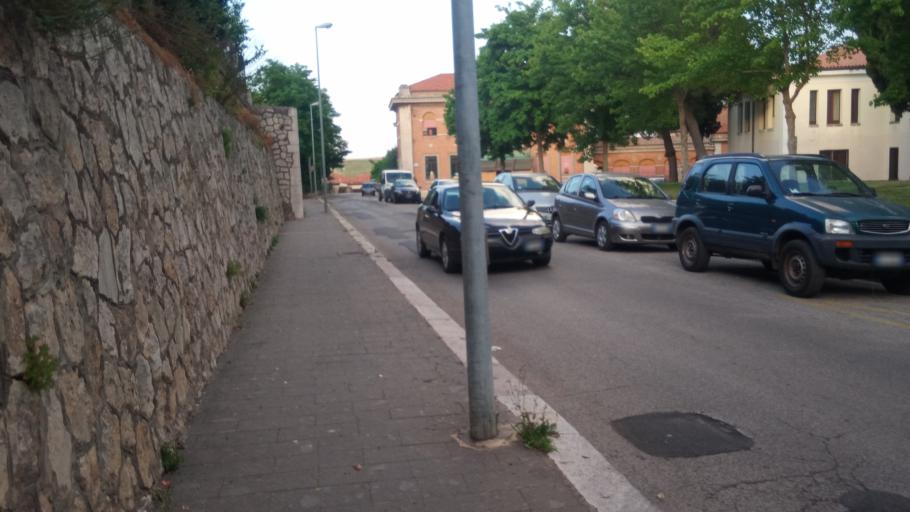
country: IT
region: Basilicate
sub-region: Provincia di Potenza
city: Melfi
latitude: 40.9971
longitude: 15.6589
